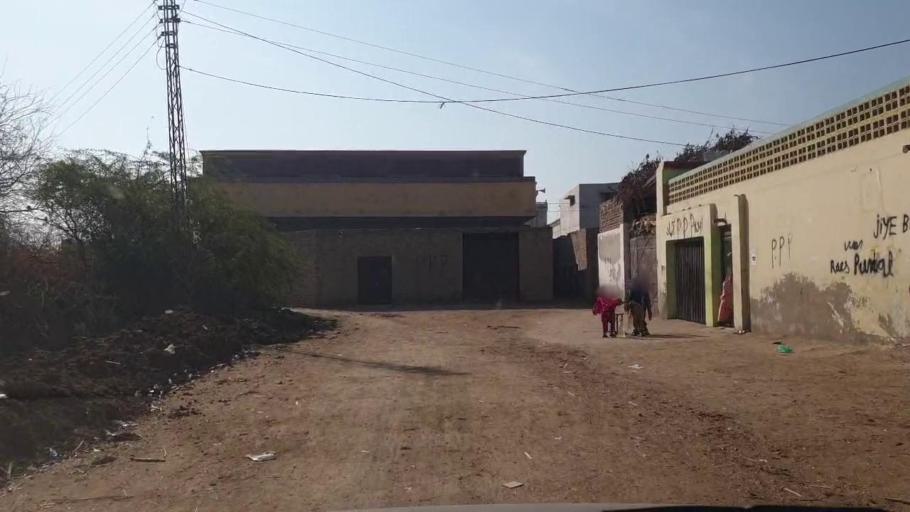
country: PK
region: Sindh
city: Tando Allahyar
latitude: 25.4065
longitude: 68.7375
